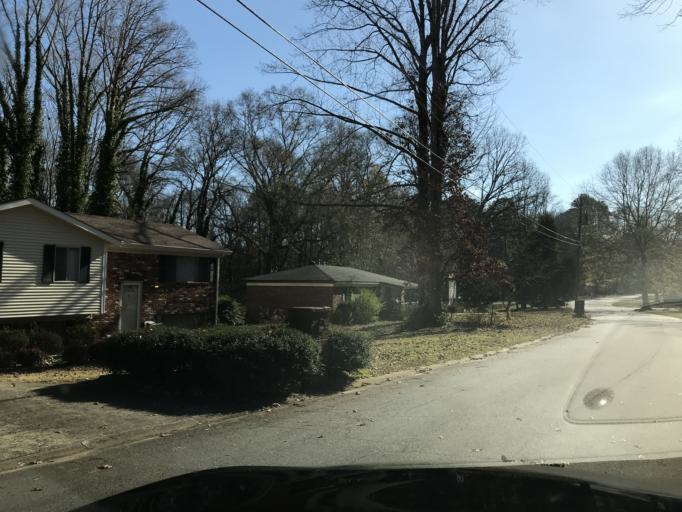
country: US
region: Georgia
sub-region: Clayton County
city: Morrow
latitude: 33.5825
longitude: -84.3714
